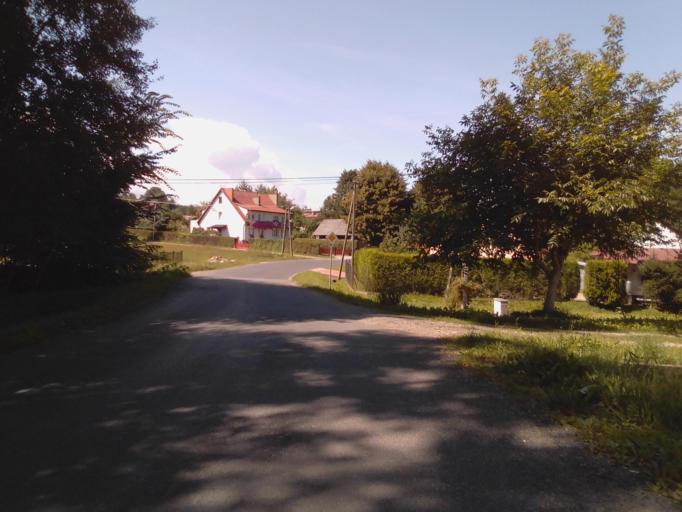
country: PL
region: Subcarpathian Voivodeship
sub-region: Powiat krosnienski
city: Jedlicze
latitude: 49.6919
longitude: 21.6147
